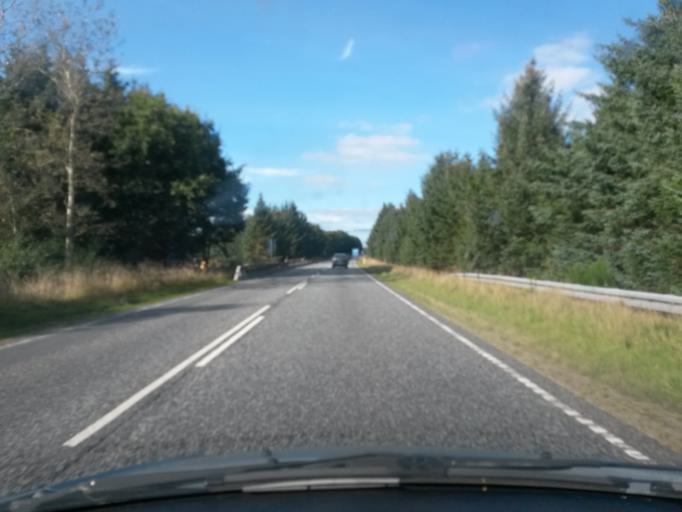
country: DK
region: Central Jutland
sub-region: Herning Kommune
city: Avlum
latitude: 56.2381
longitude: 8.8062
